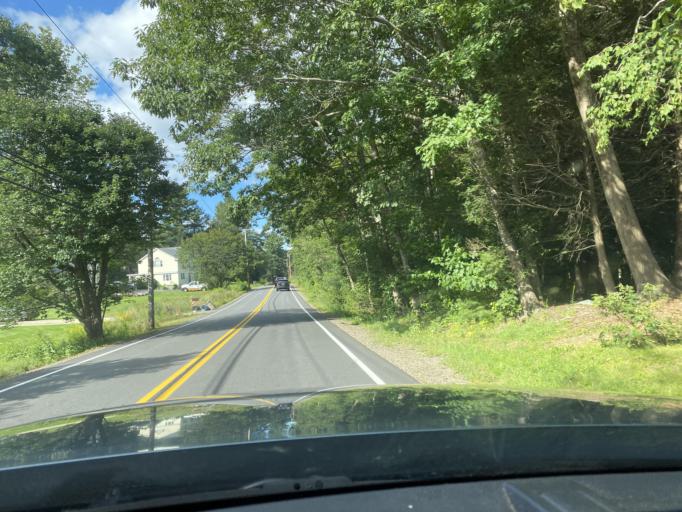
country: US
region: Maine
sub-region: York County
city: York Harbor
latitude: 43.1555
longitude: -70.7114
